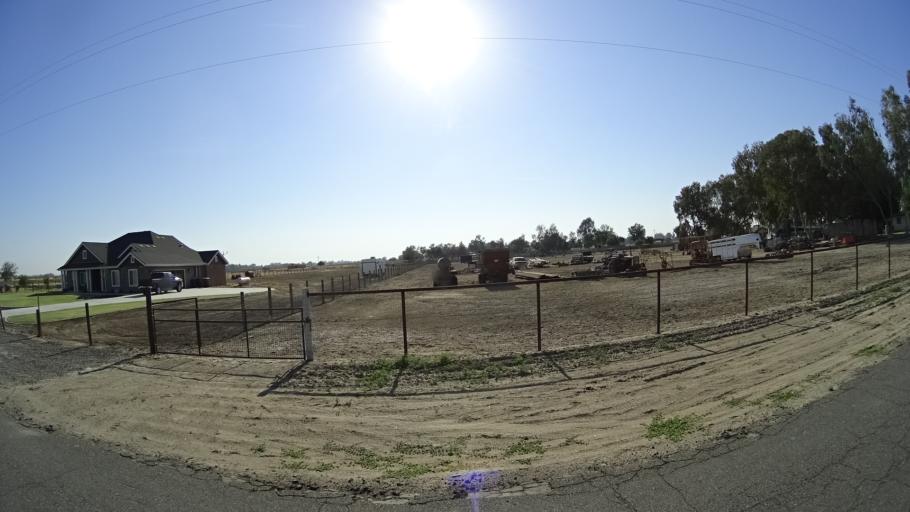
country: US
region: California
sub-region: Fresno County
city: Riverdale
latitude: 36.3525
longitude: -119.8693
